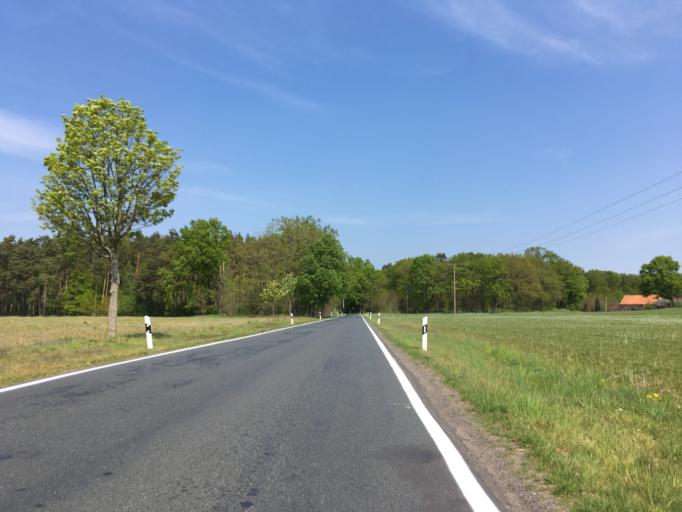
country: DE
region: Brandenburg
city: Melchow
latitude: 52.7223
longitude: 13.7124
